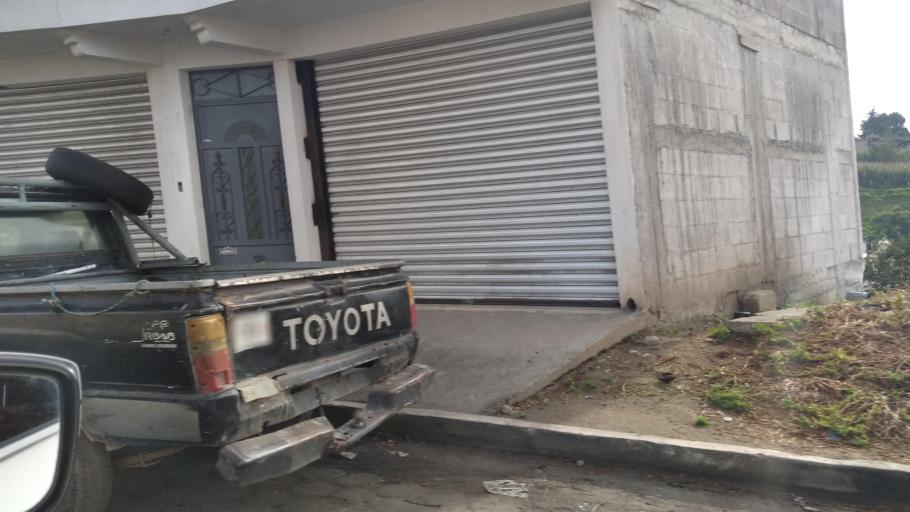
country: GT
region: Quetzaltenango
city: Quetzaltenango
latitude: 14.8539
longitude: -91.5179
